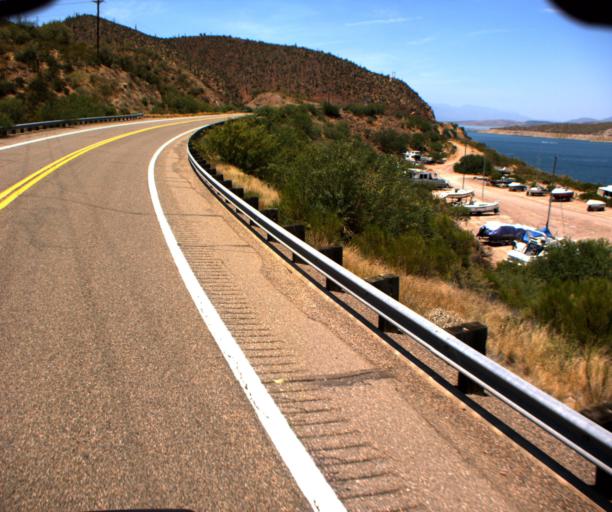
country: US
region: Arizona
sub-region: Gila County
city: Tonto Basin
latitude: 33.6675
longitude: -111.1390
